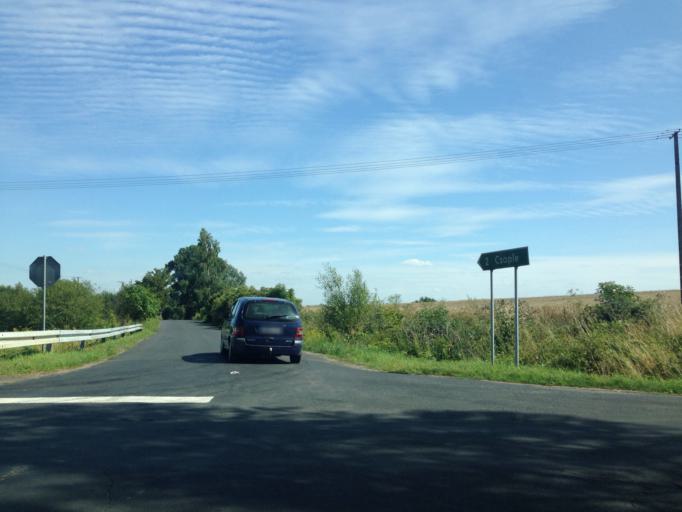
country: PL
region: Kujawsko-Pomorskie
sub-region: Powiat swiecki
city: Jezewo
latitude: 53.4631
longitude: 18.4725
